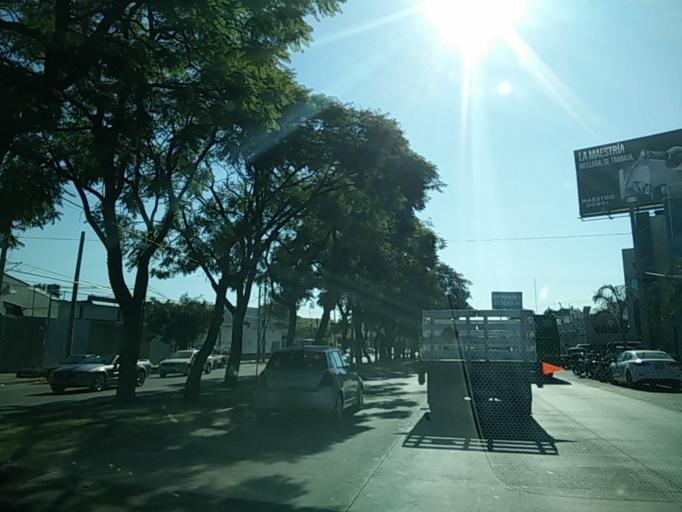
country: MX
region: Jalisco
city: Guadalajara
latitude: 20.6559
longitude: -103.3484
